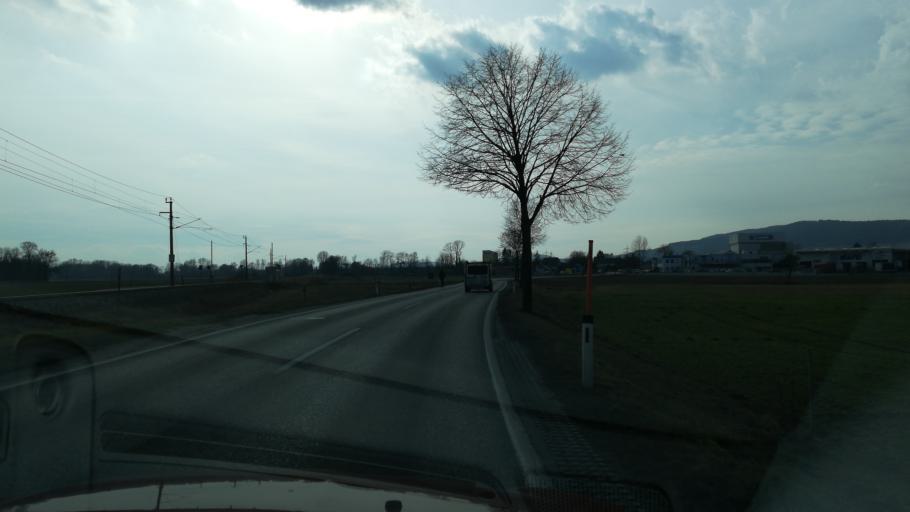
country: AT
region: Lower Austria
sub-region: Politischer Bezirk Sankt Polten
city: Traismauer
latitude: 48.3456
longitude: 15.7314
